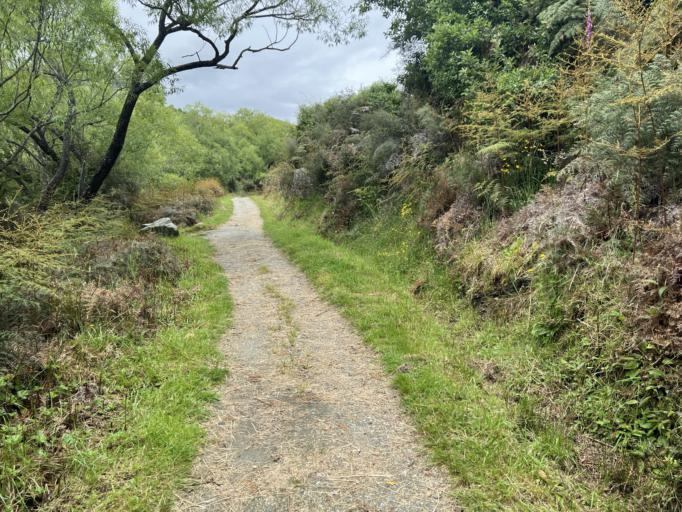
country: NZ
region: Otago
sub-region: Queenstown-Lakes District
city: Wanaka
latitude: -44.6475
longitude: 168.9624
